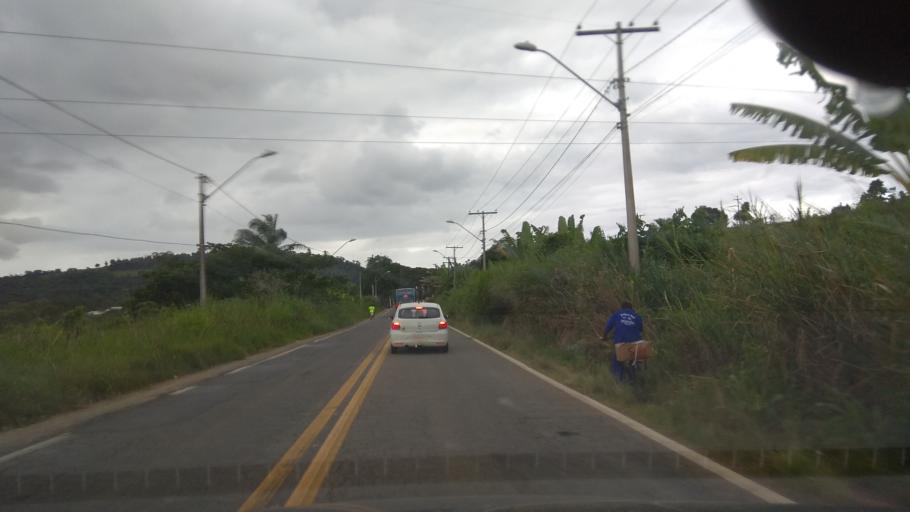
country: BR
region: Bahia
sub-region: Ubata
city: Ubata
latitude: -14.1976
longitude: -39.5405
